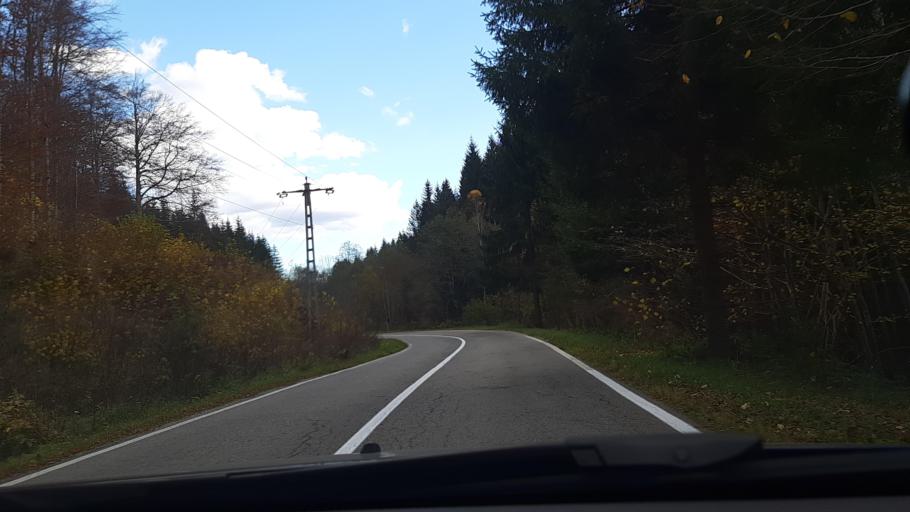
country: RO
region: Valcea
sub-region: Comuna Voineasa
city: Voineasa
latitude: 45.4358
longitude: 23.8844
